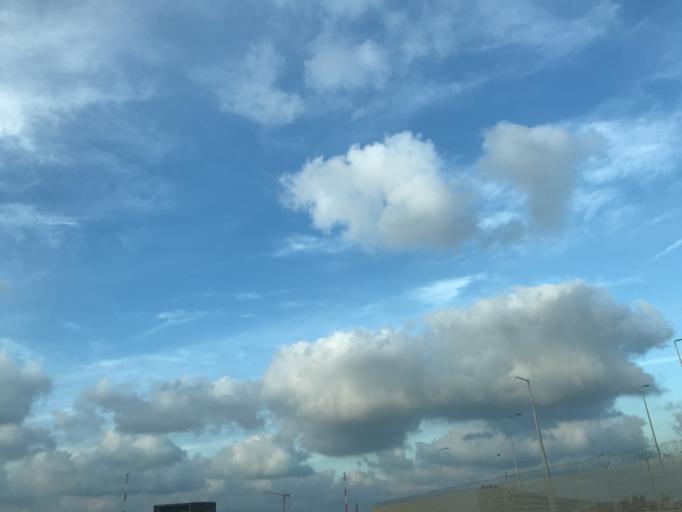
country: TR
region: Istanbul
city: Durusu
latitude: 41.2634
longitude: 28.7149
